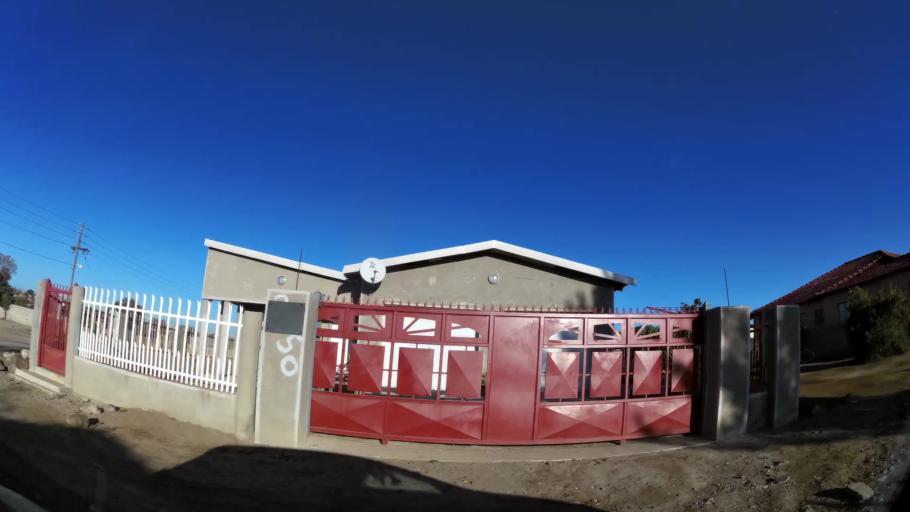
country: ZA
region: Limpopo
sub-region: Capricorn District Municipality
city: Polokwane
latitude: -23.8411
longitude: 29.3538
